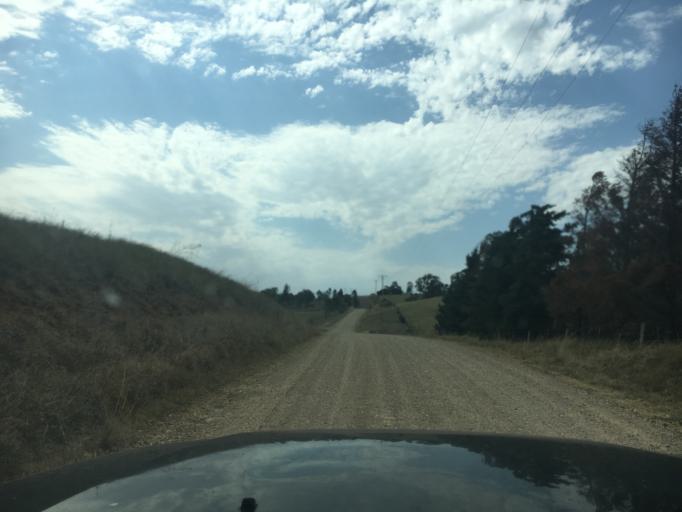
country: AU
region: New South Wales
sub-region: Cessnock
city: Branxton
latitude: -32.5055
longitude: 151.3160
